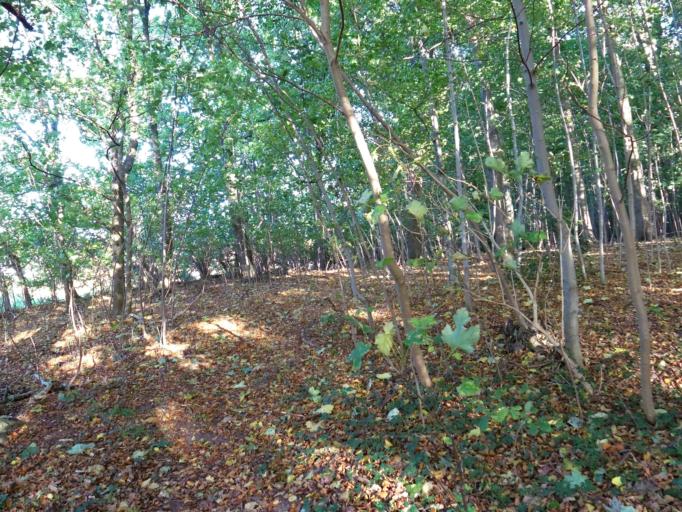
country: DK
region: Central Jutland
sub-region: Arhus Kommune
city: Stavtrup
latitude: 56.1327
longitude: 10.1366
